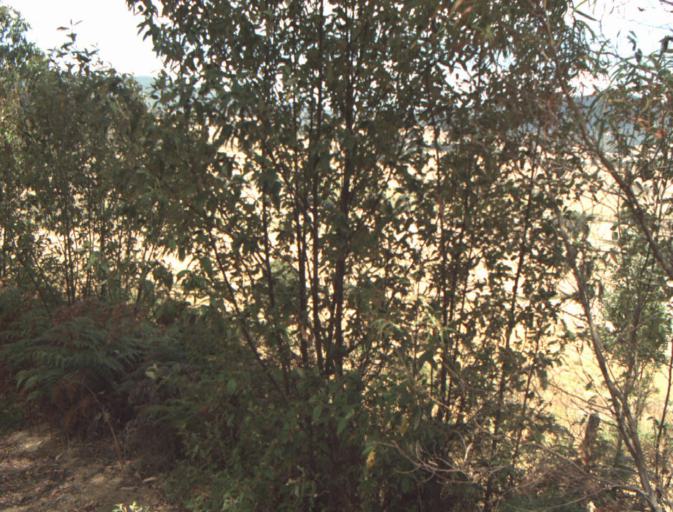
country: AU
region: Tasmania
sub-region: Launceston
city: Mayfield
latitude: -41.2050
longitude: 147.1547
